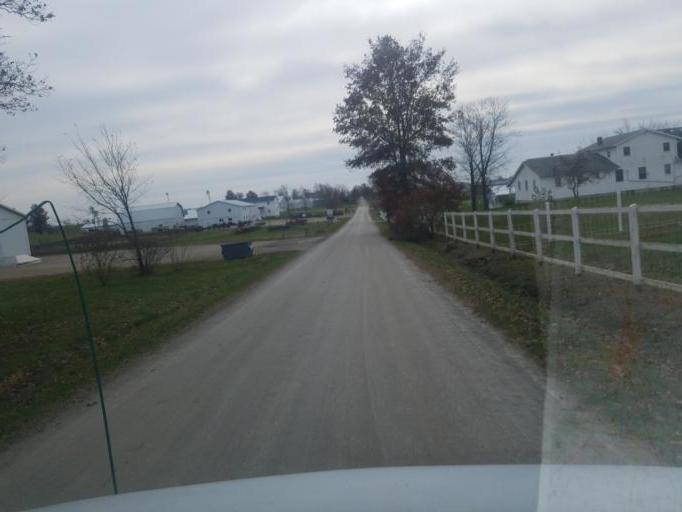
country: US
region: Indiana
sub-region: Adams County
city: Geneva
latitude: 40.6123
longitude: -84.8925
